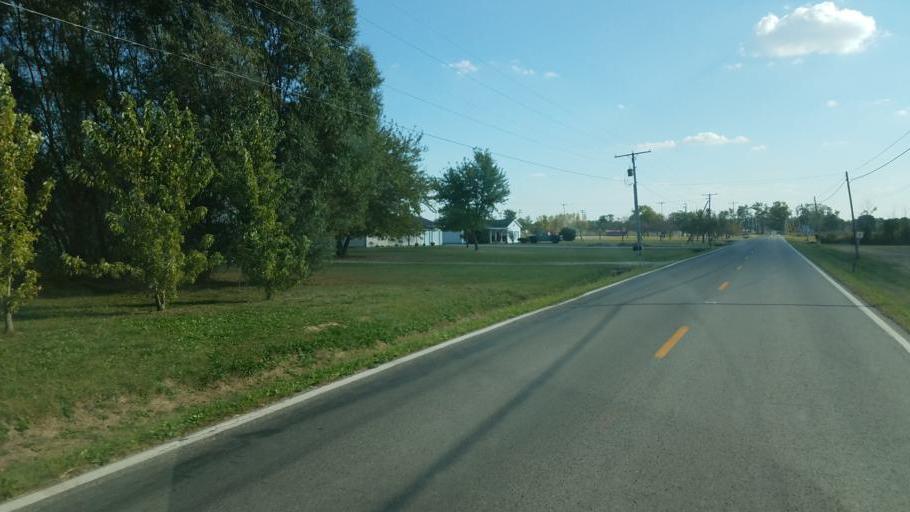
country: US
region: Ohio
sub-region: Union County
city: Richwood
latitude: 40.5911
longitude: -83.3802
